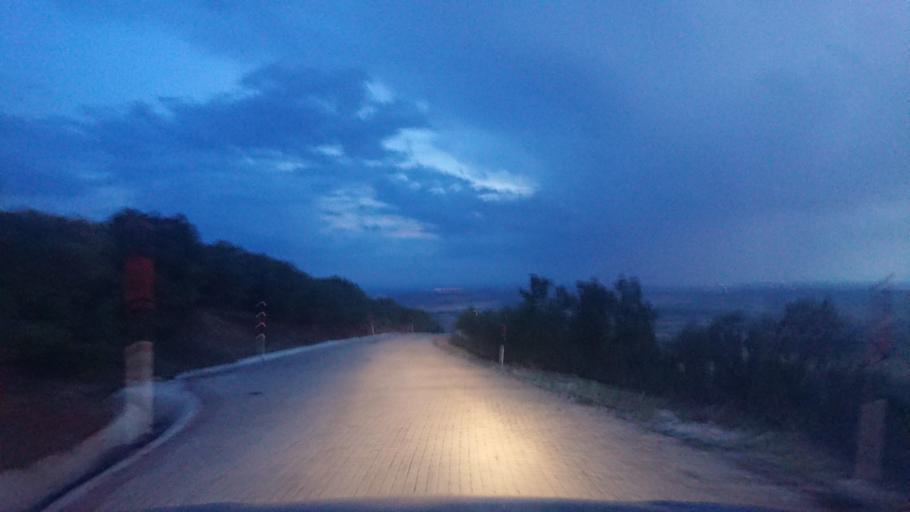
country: TR
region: Aksaray
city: Ortakoy
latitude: 38.6414
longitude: 34.0193
